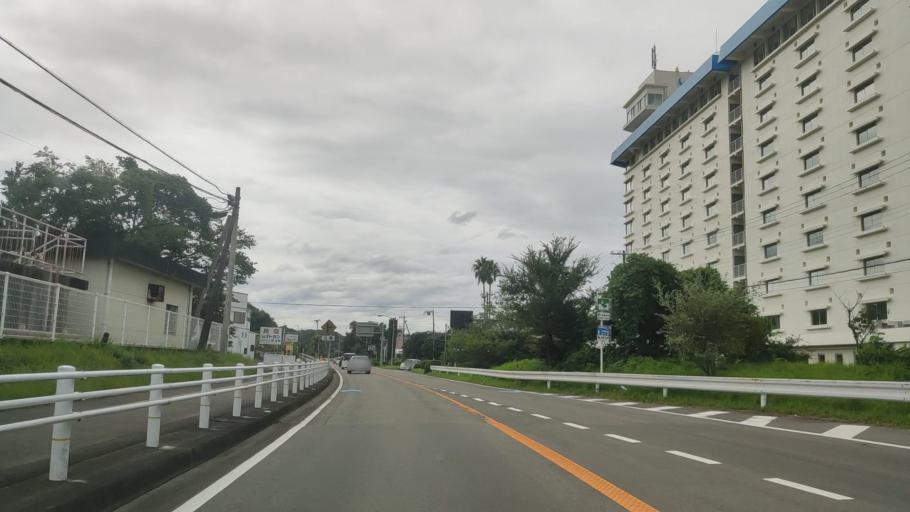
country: JP
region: Wakayama
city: Tanabe
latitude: 33.6997
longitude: 135.3888
